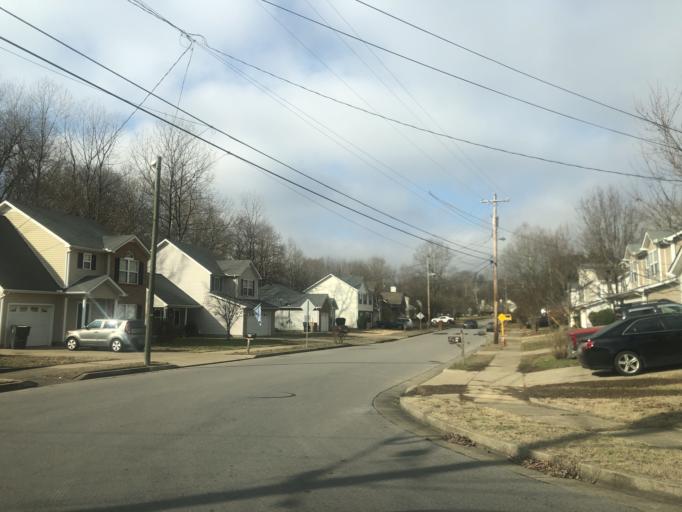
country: US
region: Tennessee
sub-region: Rutherford County
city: La Vergne
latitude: 36.0756
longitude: -86.6551
